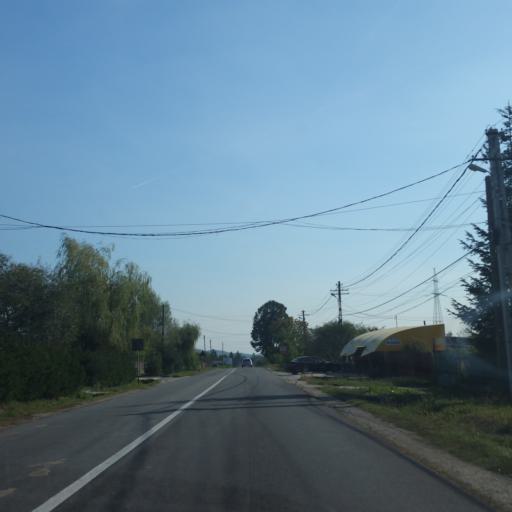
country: RO
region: Arges
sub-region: Comuna Baiculesti
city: Baiculesti
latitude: 45.0719
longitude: 24.6862
